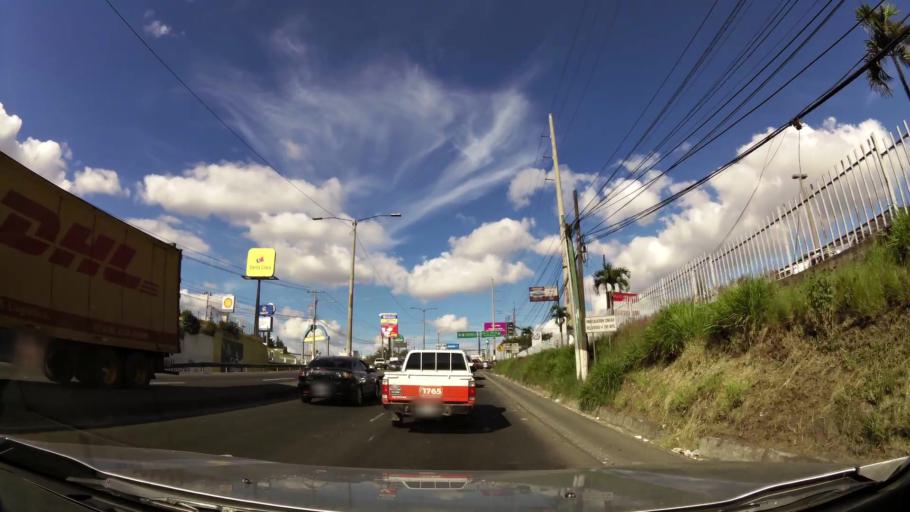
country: GT
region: Guatemala
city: Villa Nueva
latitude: 14.5294
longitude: -90.5962
